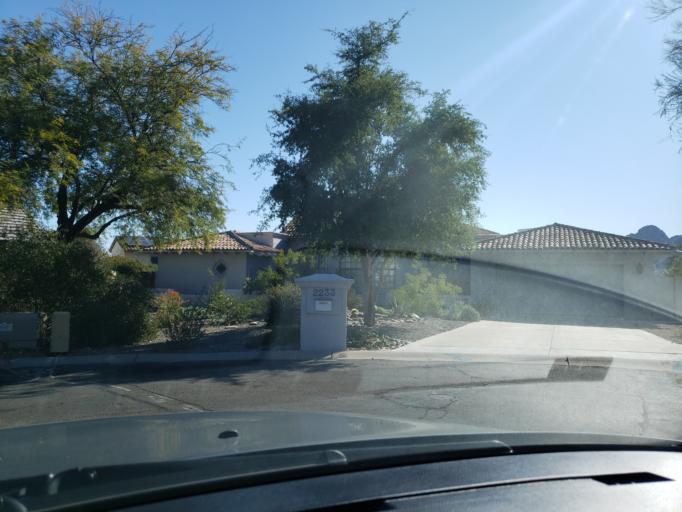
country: US
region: Arizona
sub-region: Maricopa County
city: Paradise Valley
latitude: 33.5745
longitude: -112.0334
